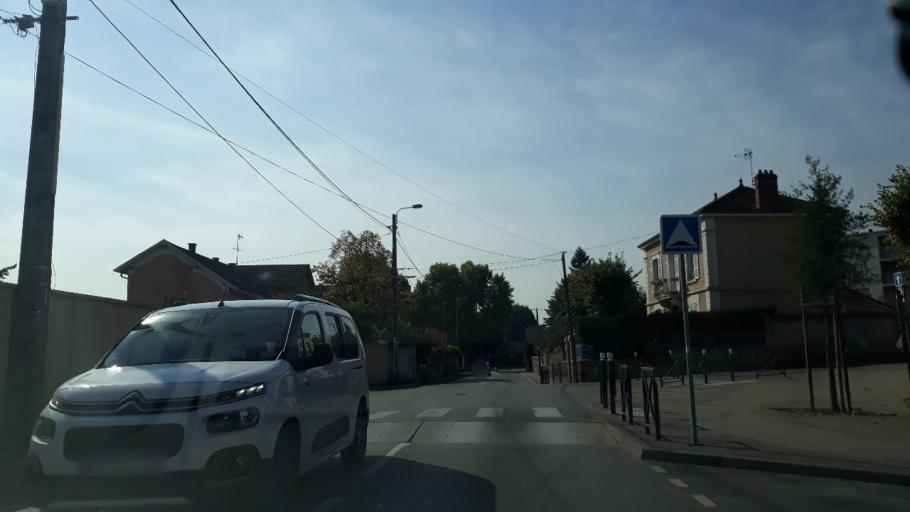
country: FR
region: Rhone-Alpes
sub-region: Departement du Rhone
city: Villefranche-sur-Saone
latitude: 45.9925
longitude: 4.7336
